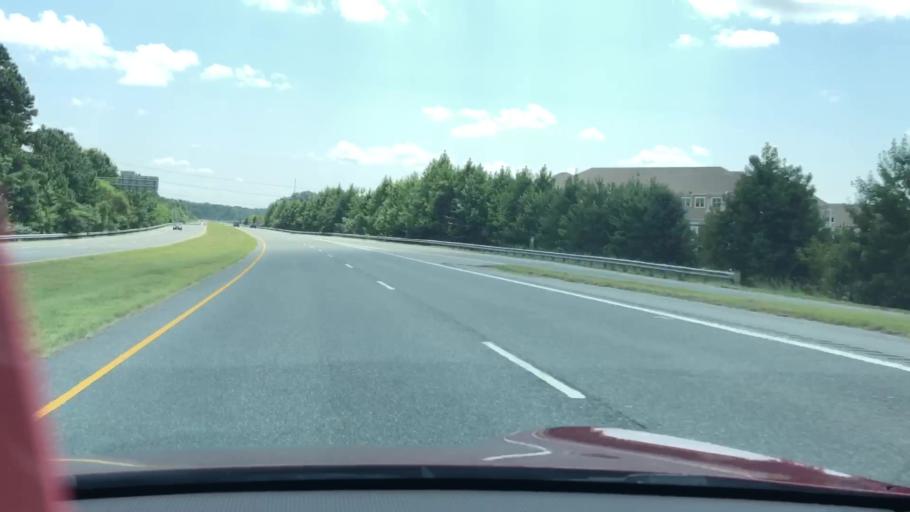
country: US
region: North Carolina
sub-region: Currituck County
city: Moyock
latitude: 36.6543
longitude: -76.2283
